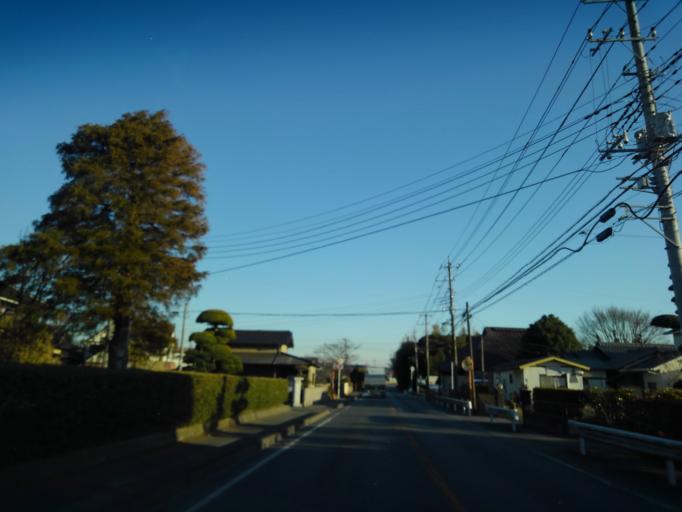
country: JP
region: Chiba
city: Kimitsu
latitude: 35.3175
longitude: 139.9298
